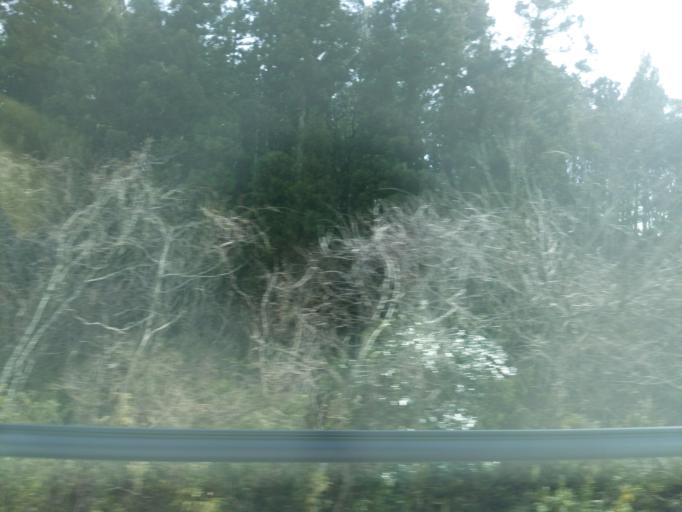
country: JP
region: Miyagi
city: Furukawa
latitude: 38.6317
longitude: 141.0050
